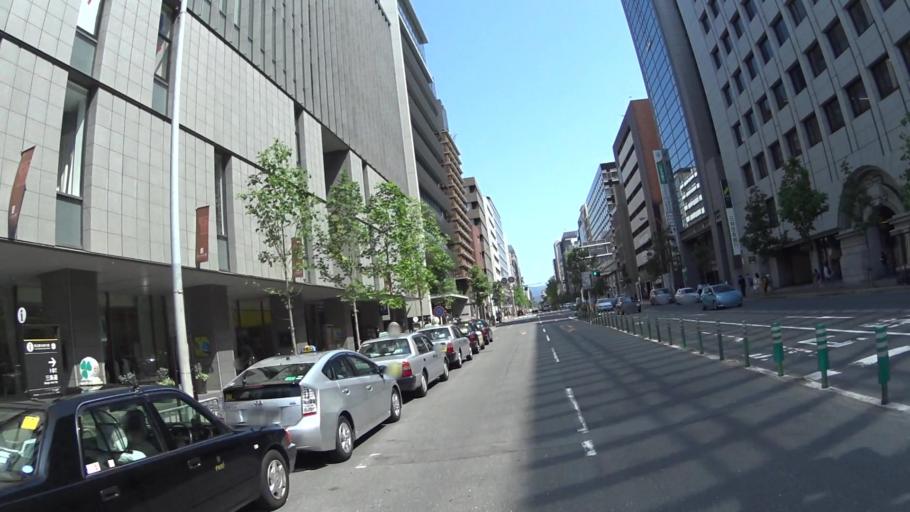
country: JP
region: Kyoto
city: Kyoto
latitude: 35.0039
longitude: 135.7597
